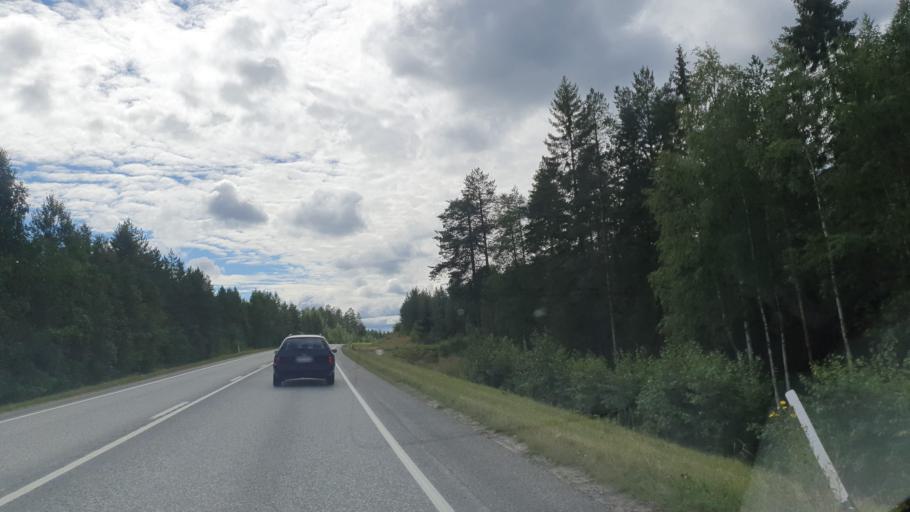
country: FI
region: Kainuu
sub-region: Kajaani
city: Kajaani
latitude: 64.1967
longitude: 27.6287
